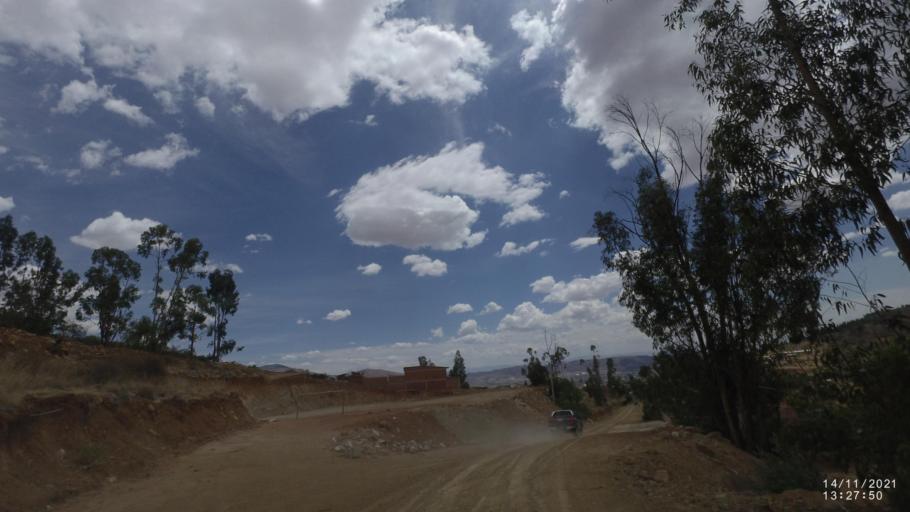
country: BO
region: Cochabamba
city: Colomi
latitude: -17.3843
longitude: -65.9821
